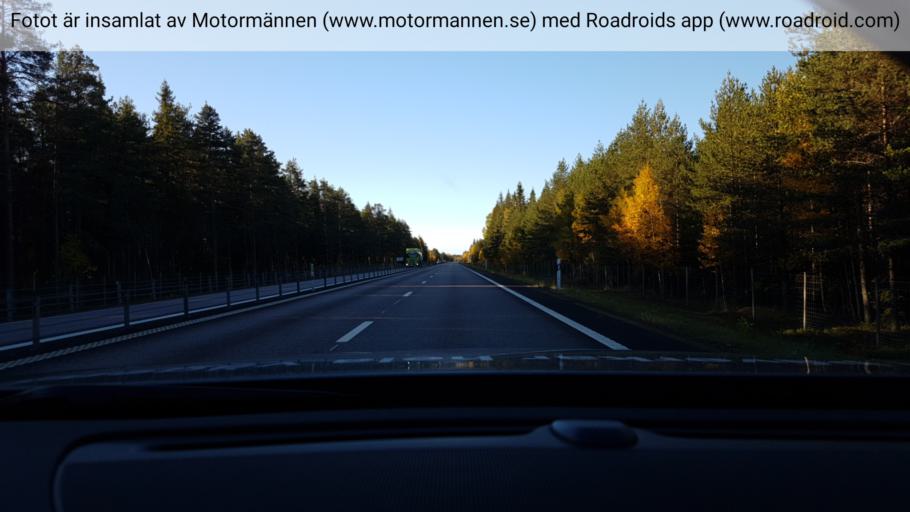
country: SE
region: Norrbotten
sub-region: Pitea Kommun
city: Rosvik
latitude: 65.5058
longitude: 21.7719
